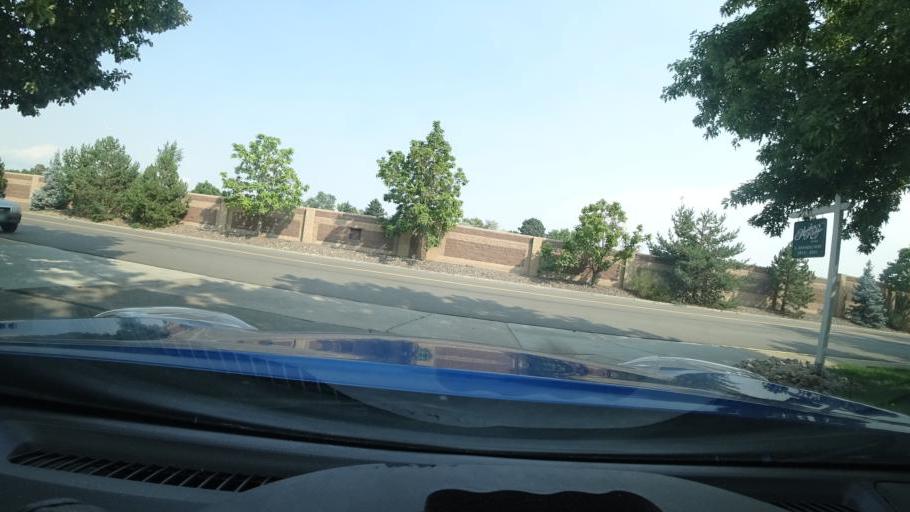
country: US
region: Colorado
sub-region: Adams County
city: Aurora
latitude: 39.6649
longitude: -104.8333
